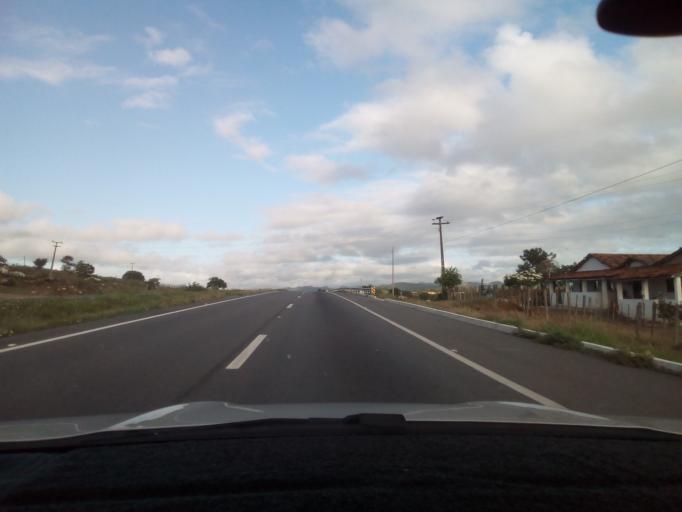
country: BR
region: Paraiba
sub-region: Serra Redonda
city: Alagoa Grande
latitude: -7.2033
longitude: -35.5454
